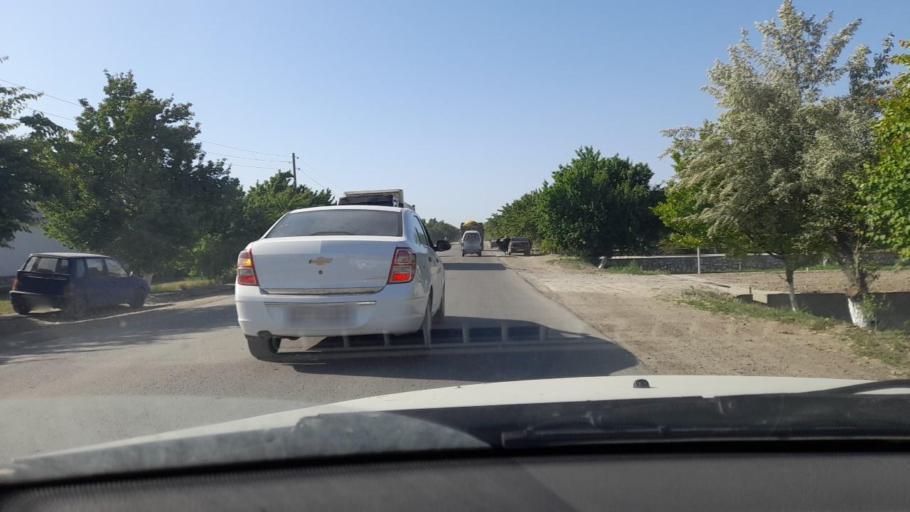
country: UZ
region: Bukhara
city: Romiton
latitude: 40.0578
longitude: 64.3278
